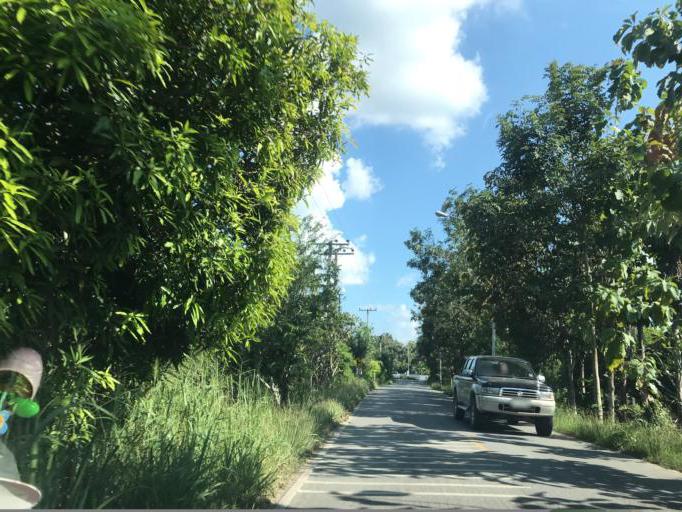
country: TH
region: Lamphun
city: Pa Sang
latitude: 18.5314
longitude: 98.8441
